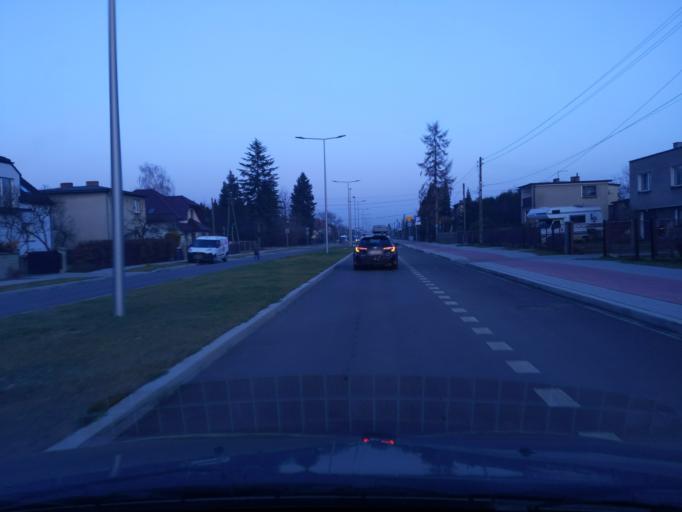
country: PL
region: Silesian Voivodeship
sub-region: Powiat pszczynski
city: Pszczyna
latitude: 49.9674
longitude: 18.9316
